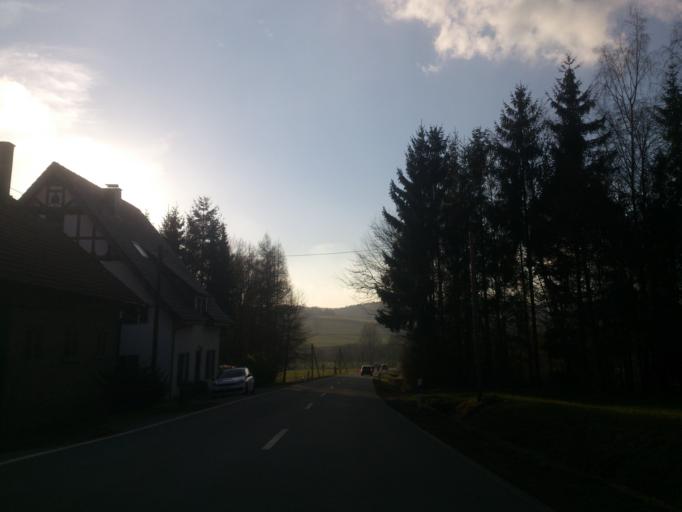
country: DE
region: North Rhine-Westphalia
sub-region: Regierungsbezirk Detmold
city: Bad Driburg
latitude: 51.7386
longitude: 9.0690
